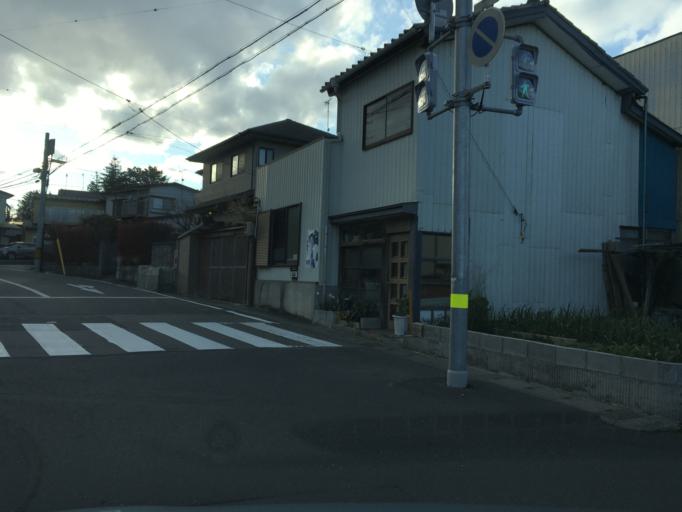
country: JP
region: Miyagi
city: Ishinomaki
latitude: 38.4308
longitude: 141.3003
